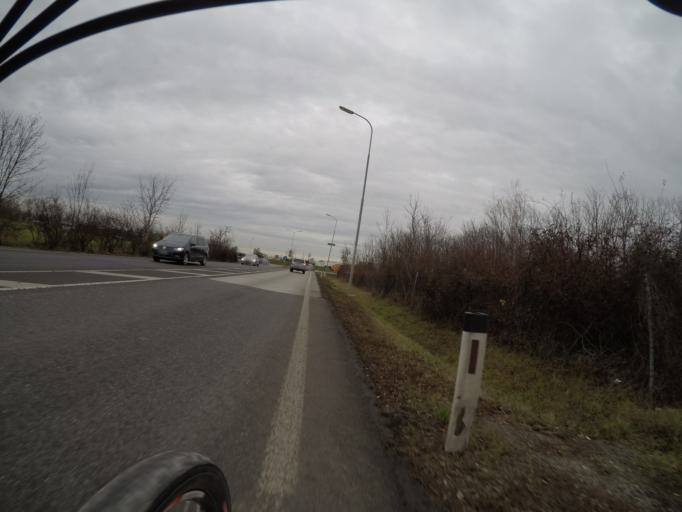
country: AT
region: Lower Austria
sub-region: Politischer Bezirk Modling
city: Wiener Neudorf
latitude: 48.1037
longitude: 16.3110
